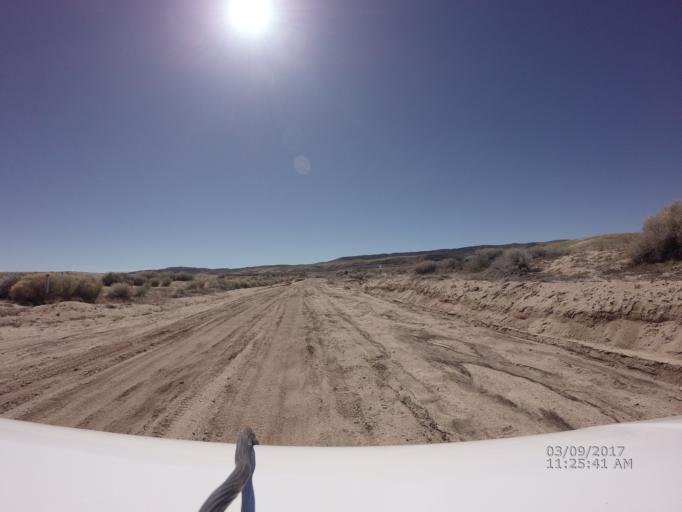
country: US
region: California
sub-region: Los Angeles County
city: Green Valley
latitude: 34.7076
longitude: -118.3949
